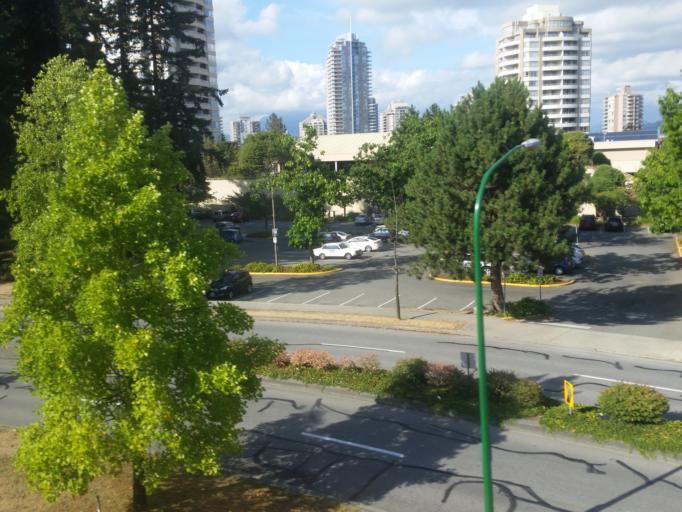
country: CA
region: British Columbia
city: Burnaby
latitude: 49.2228
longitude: -122.9975
